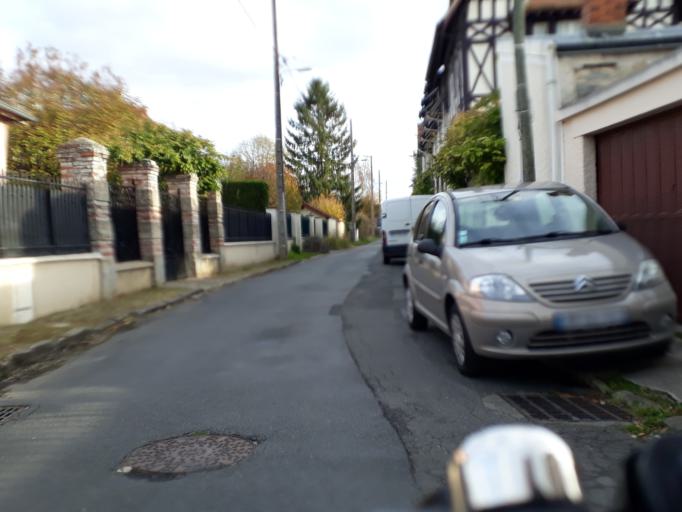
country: FR
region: Ile-de-France
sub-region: Departement de Seine-et-Marne
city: Bois-le-Roi
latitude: 48.4658
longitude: 2.6978
